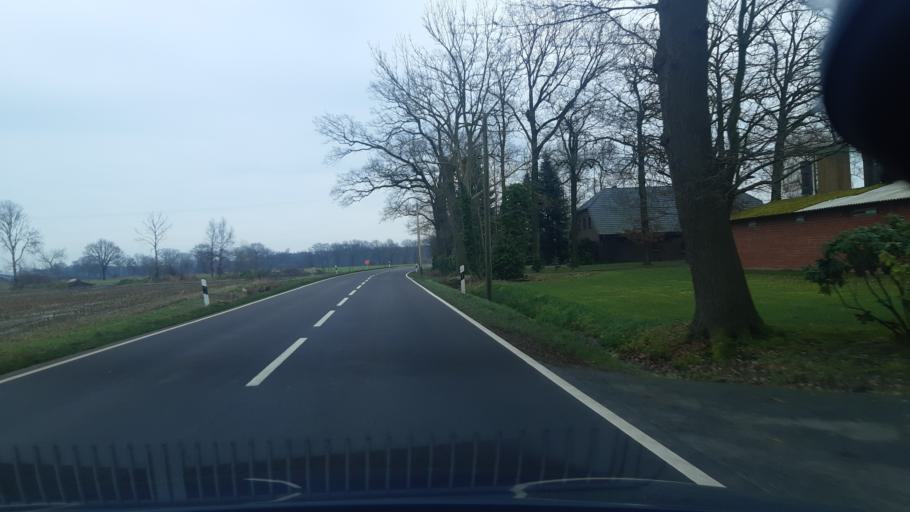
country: DE
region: Lower Saxony
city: Cloppenburg
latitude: 52.8176
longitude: 8.0087
